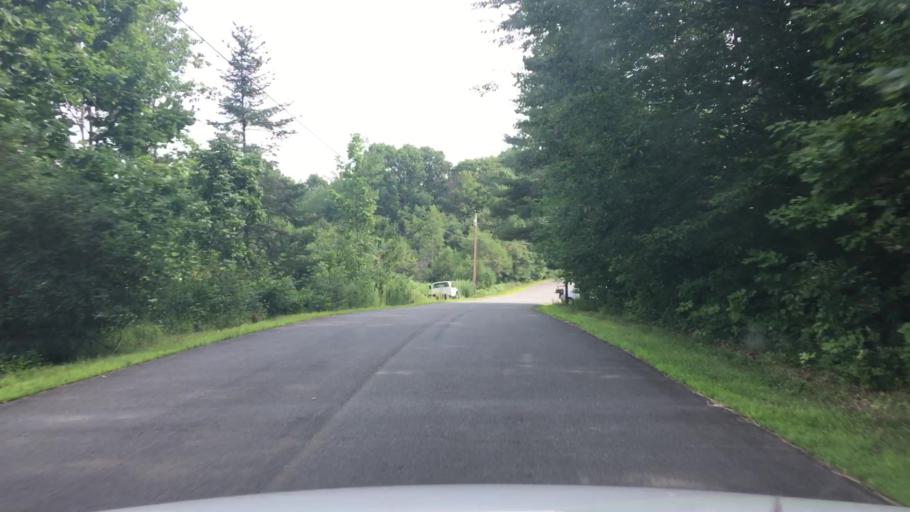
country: US
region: Maine
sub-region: Lincoln County
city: Jefferson
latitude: 44.2346
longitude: -69.4440
